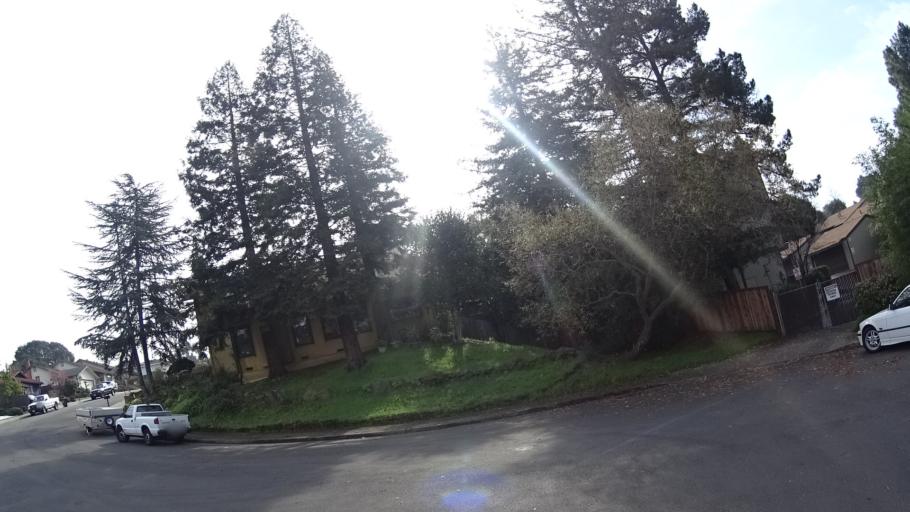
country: US
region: California
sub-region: Alameda County
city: Fairview
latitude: 37.6812
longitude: -122.0606
